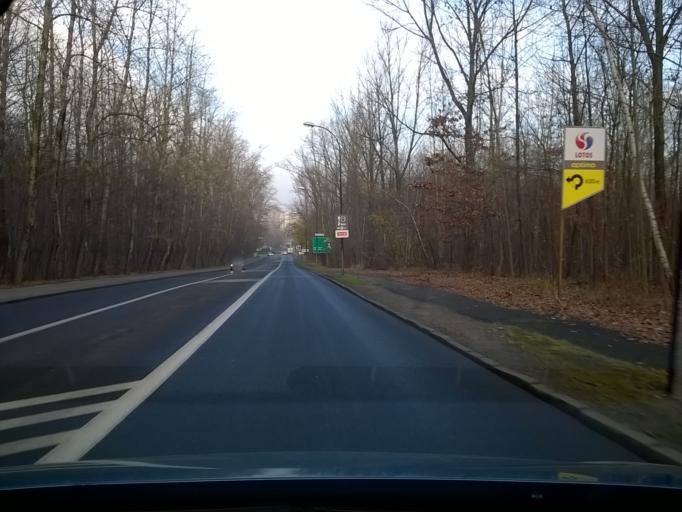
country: PL
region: Silesian Voivodeship
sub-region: Swietochlowice
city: Swietochlowice
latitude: 50.2565
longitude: 18.9364
